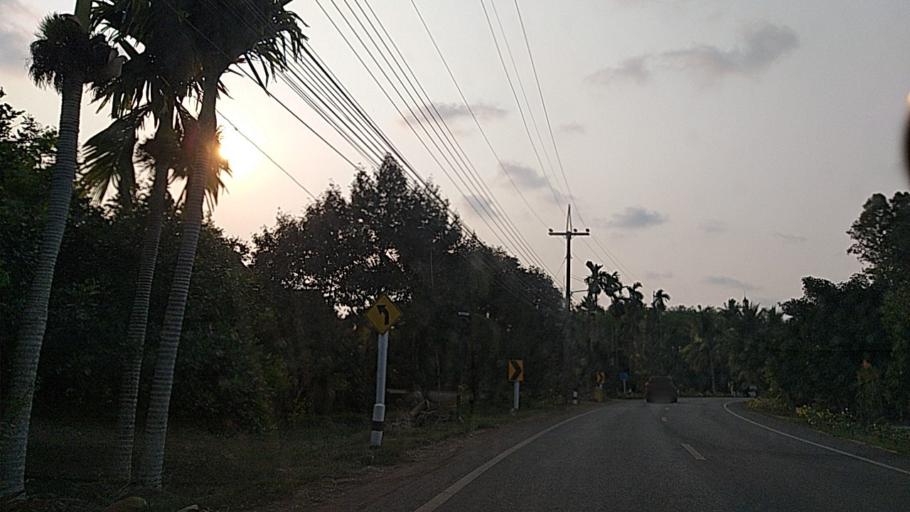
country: TH
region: Trat
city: Laem Ngop
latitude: 12.2147
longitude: 102.3029
